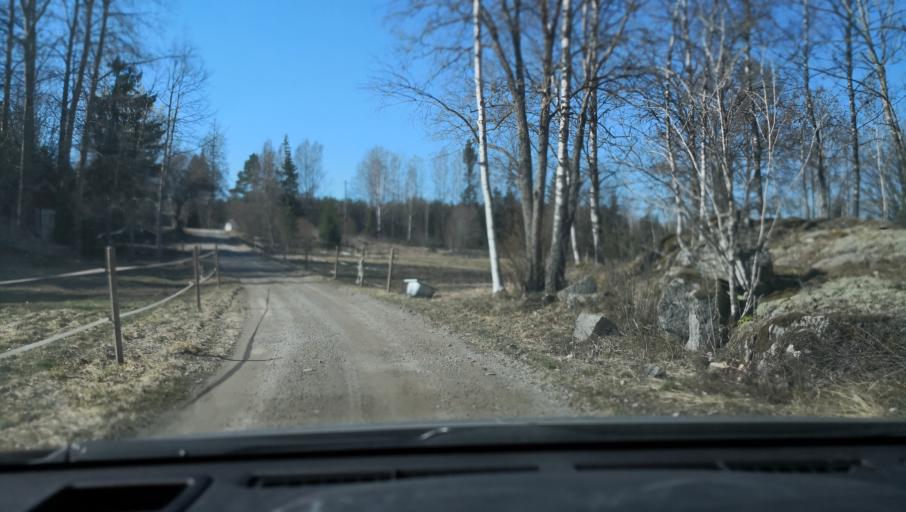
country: SE
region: Vaestmanland
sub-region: Sala Kommun
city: Sala
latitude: 59.9443
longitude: 16.4383
